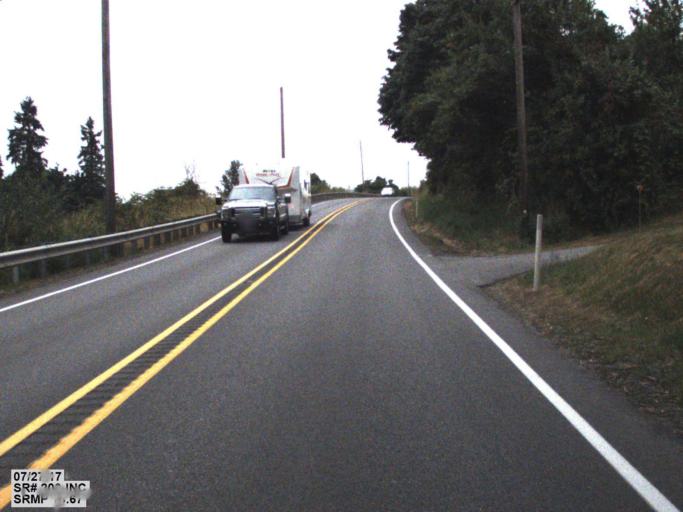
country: US
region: Washington
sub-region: King County
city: Duvall
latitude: 47.7239
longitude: -121.9865
